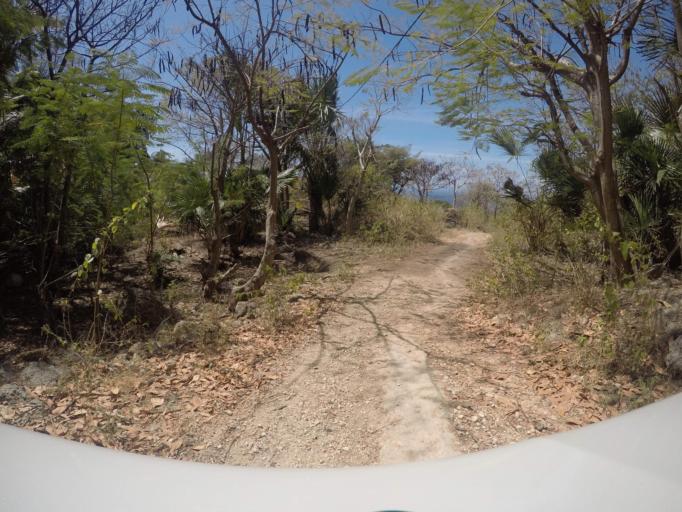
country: TL
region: Baucau
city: Baucau
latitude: -8.4445
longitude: 126.4403
